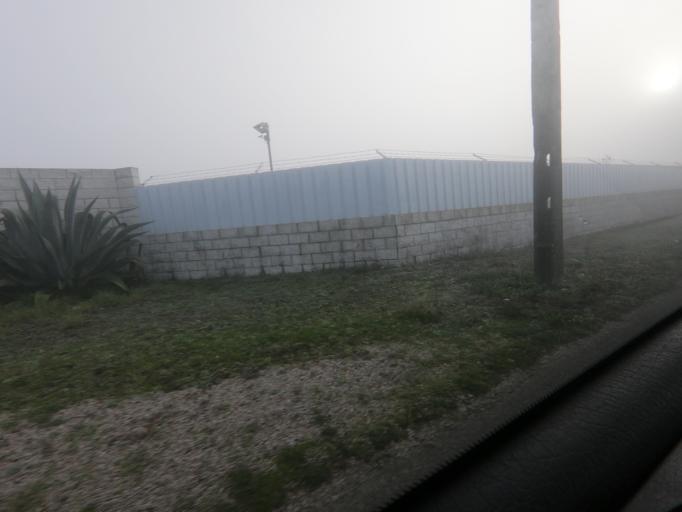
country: PT
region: Setubal
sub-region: Palmela
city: Palmela
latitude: 38.5966
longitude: -8.8435
